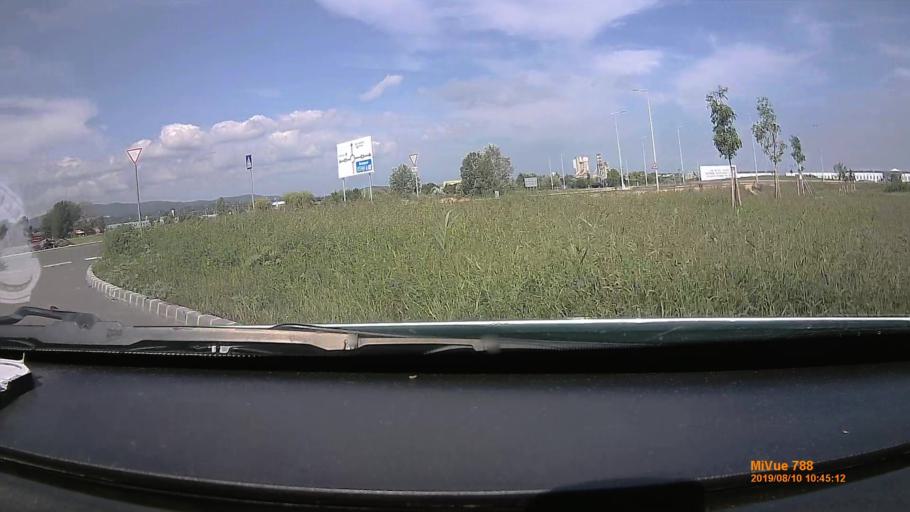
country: HU
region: Borsod-Abauj-Zemplen
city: Malyi
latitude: 48.0543
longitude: 20.8098
